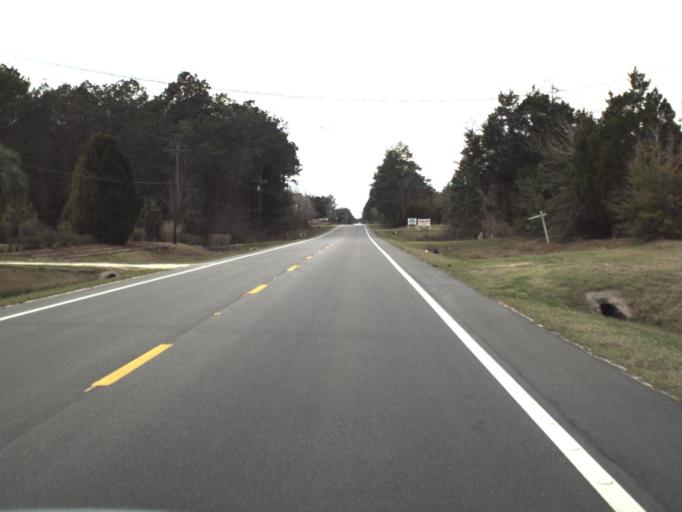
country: US
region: Florida
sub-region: Gulf County
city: Wewahitchka
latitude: 30.1211
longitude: -85.2147
